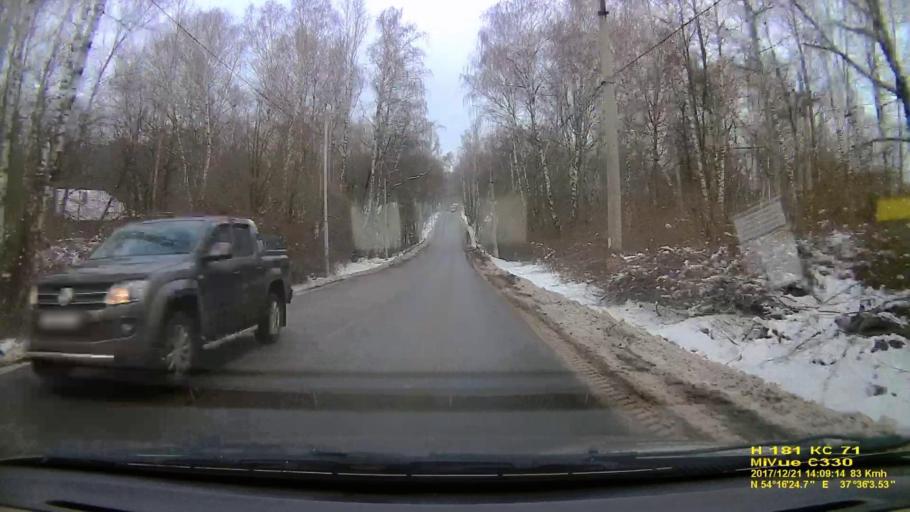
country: RU
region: Tula
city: Gorelki
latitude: 54.2737
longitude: 37.6012
